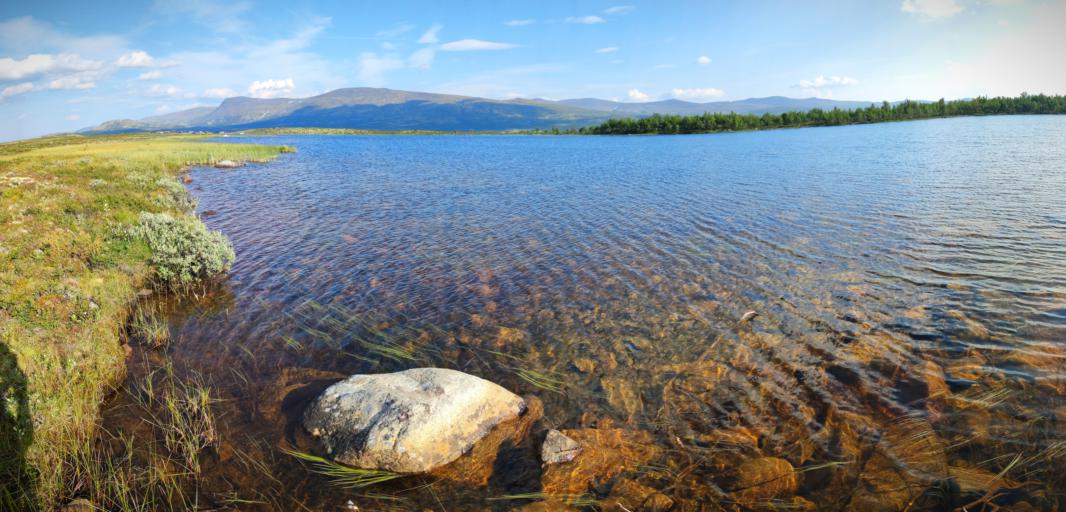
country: NO
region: Oppland
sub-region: Dovre
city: Dovre
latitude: 62.1584
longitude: 9.2812
